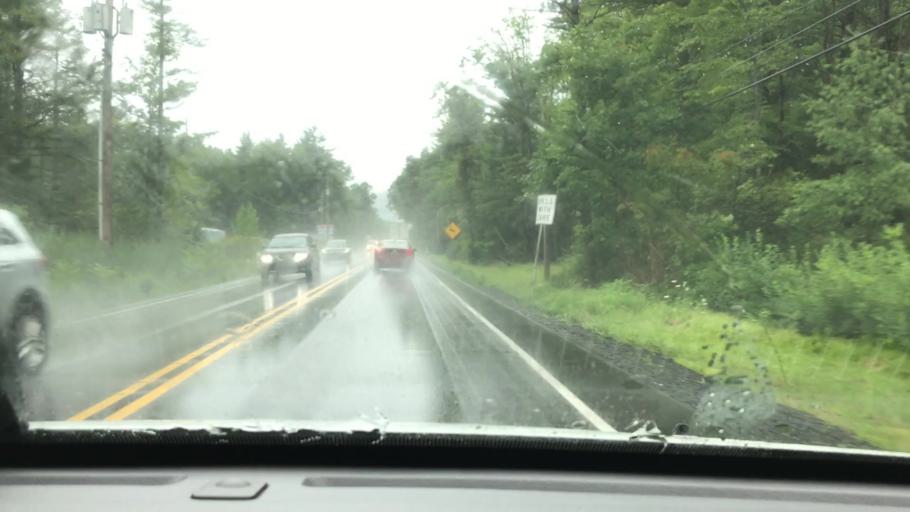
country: US
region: Pennsylvania
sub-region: Blair County
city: Tyrone
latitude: 40.7287
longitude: -78.1895
